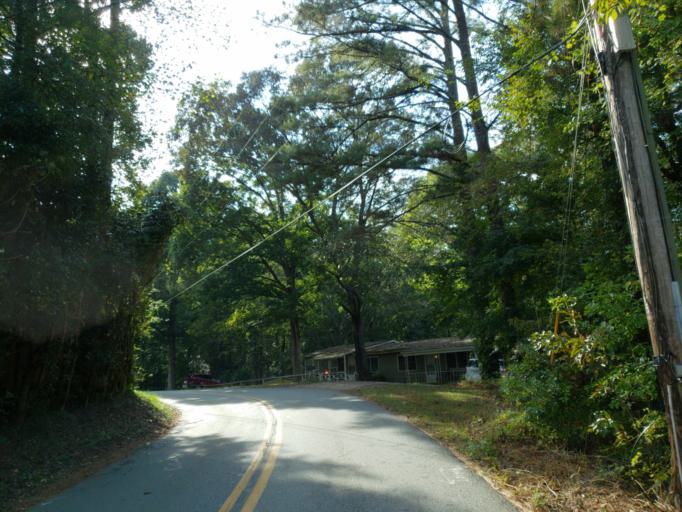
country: US
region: Georgia
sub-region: Fulton County
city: Roswell
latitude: 34.0848
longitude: -84.4229
